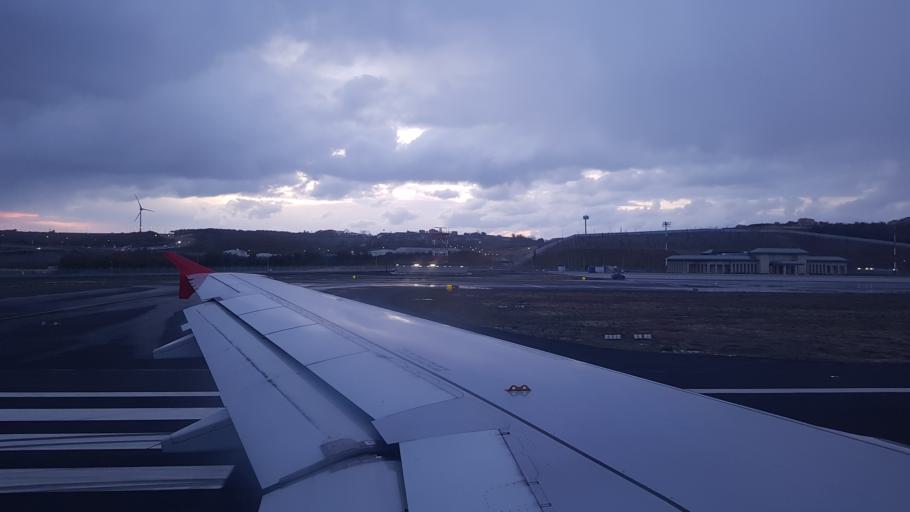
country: TR
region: Istanbul
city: Durusu
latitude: 41.2652
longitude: 28.7073
